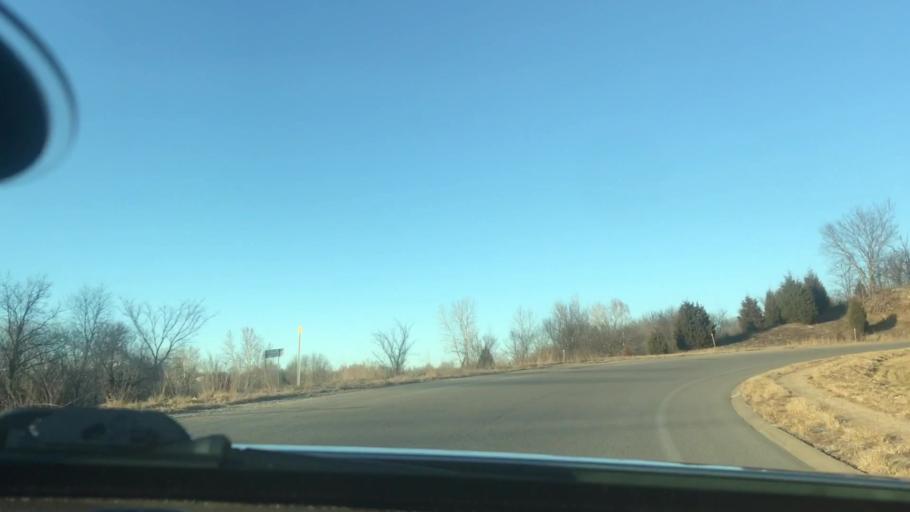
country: US
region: Missouri
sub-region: Platte County
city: Weatherby Lake
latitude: 39.2465
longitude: -94.7574
